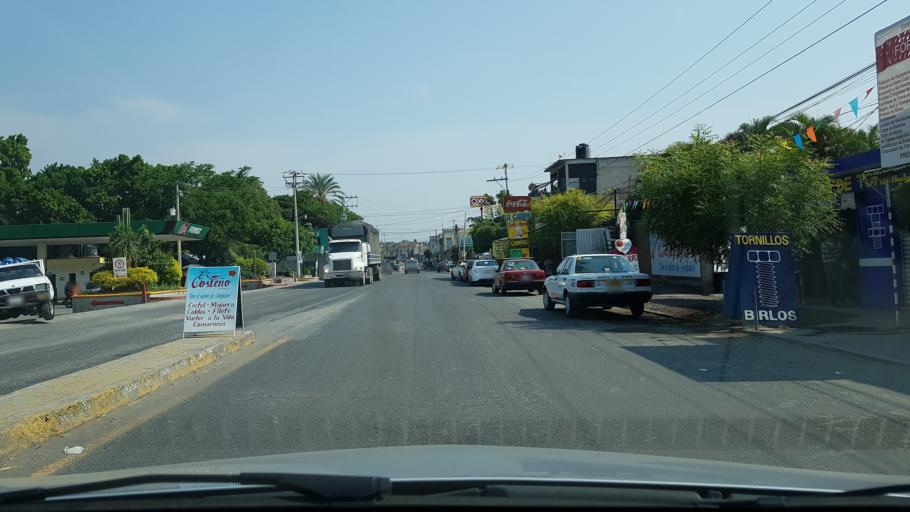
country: MX
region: Morelos
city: Zacatepec
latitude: 18.6672
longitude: -99.1861
